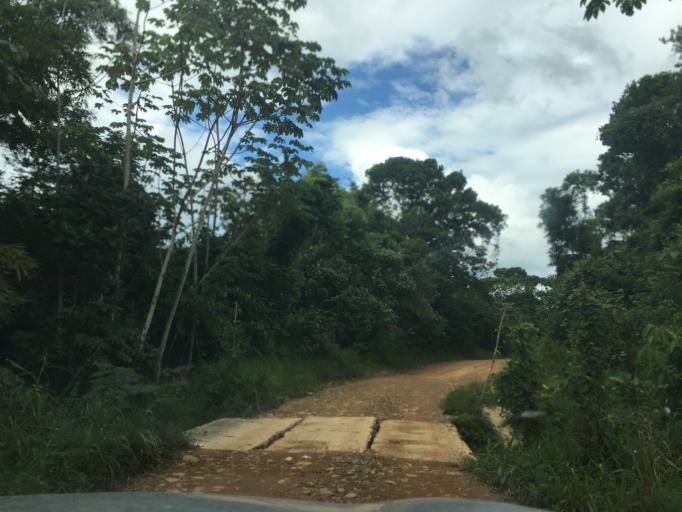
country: BZ
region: Stann Creek
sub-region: Dangriga
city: Dangriga
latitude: 16.9254
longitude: -88.3511
